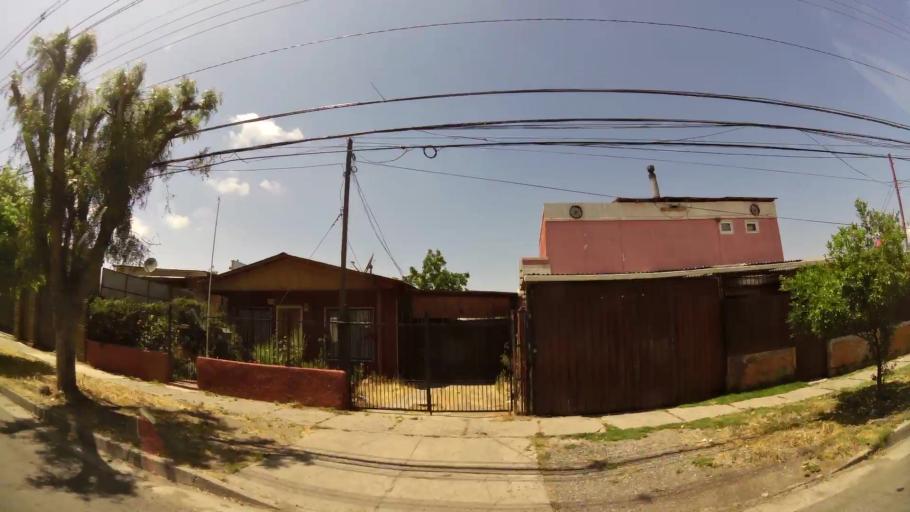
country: CL
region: Santiago Metropolitan
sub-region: Provincia de Maipo
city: San Bernardo
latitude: -33.5694
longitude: -70.7880
